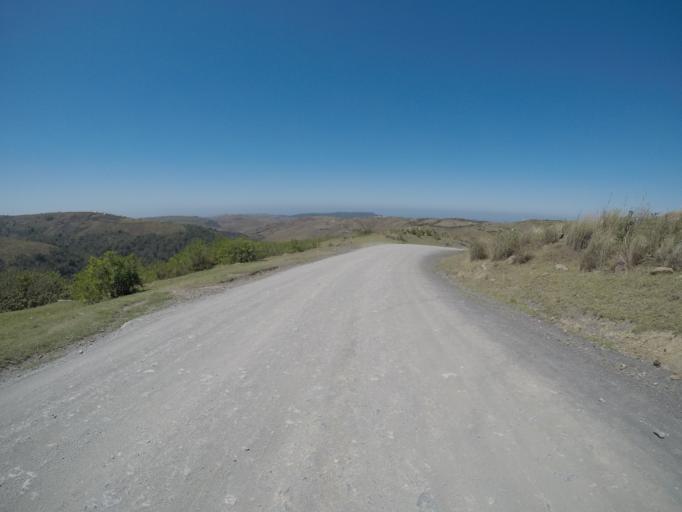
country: ZA
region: Eastern Cape
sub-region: OR Tambo District Municipality
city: Libode
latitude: -31.9761
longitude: 29.0352
